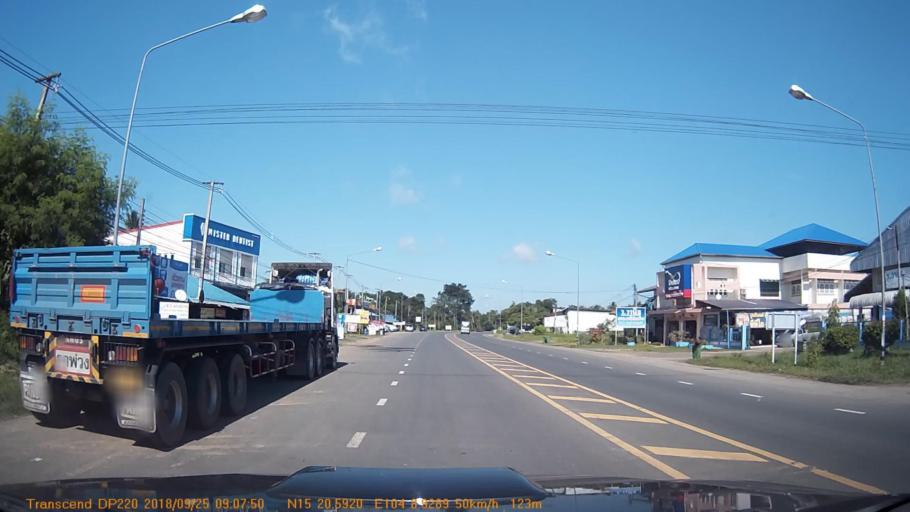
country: TH
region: Sisaket
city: Rasi Salai
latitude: 15.3432
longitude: 104.1490
